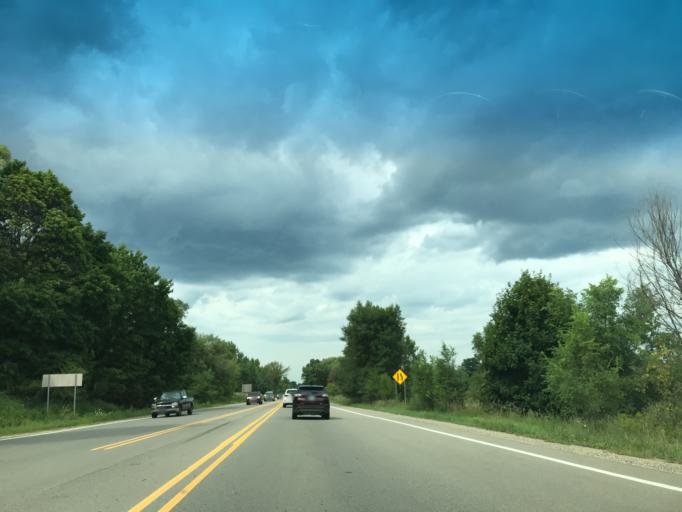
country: US
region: Michigan
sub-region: Oakland County
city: South Lyon
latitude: 42.5233
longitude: -83.6158
